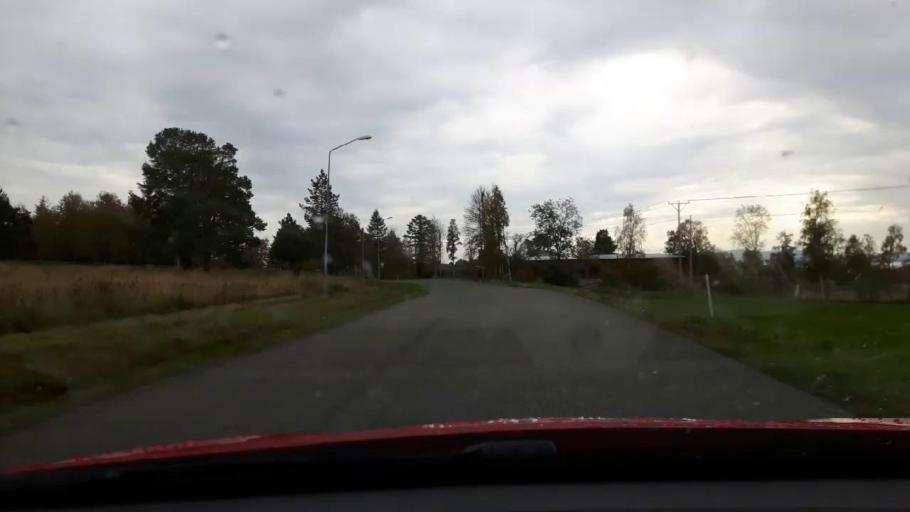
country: SE
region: Jaemtland
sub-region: Bergs Kommun
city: Hoverberg
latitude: 62.9493
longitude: 14.4911
